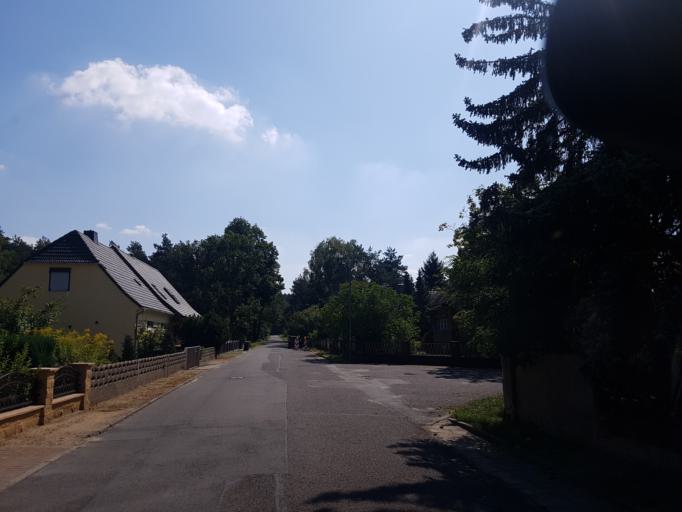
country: DE
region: Brandenburg
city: Elsterwerda
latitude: 51.4999
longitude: 13.4988
